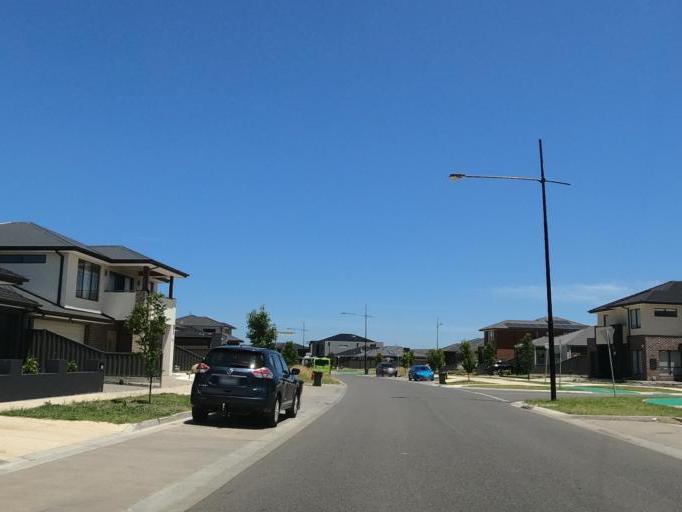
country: AU
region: Victoria
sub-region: Hume
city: Roxburgh Park
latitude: -37.6219
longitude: 144.9169
